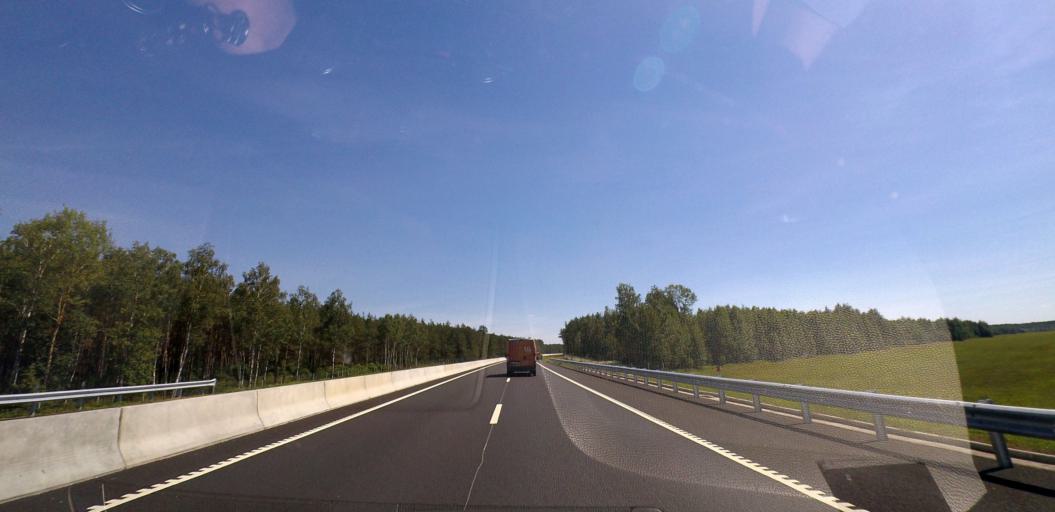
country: BY
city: Berezovka
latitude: 53.8424
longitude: 25.4848
